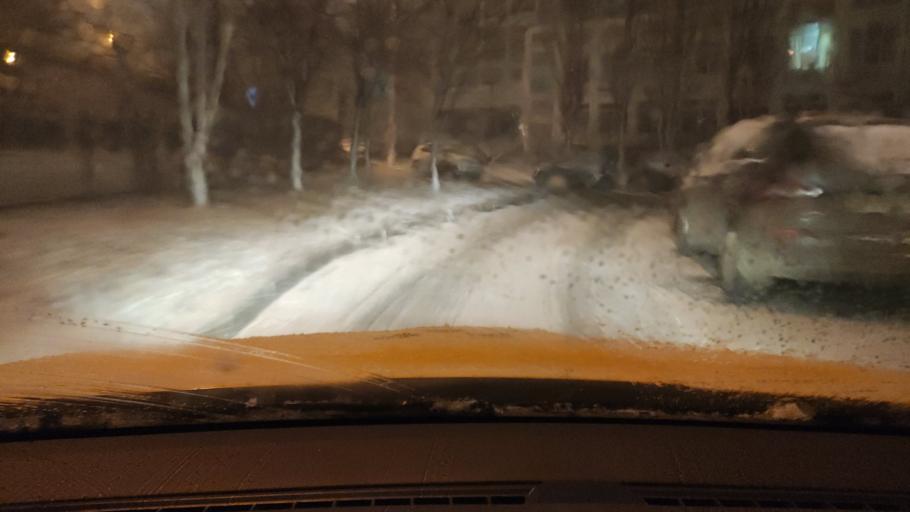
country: RU
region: Moskovskaya
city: Kozhukhovo
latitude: 55.7010
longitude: 37.6857
